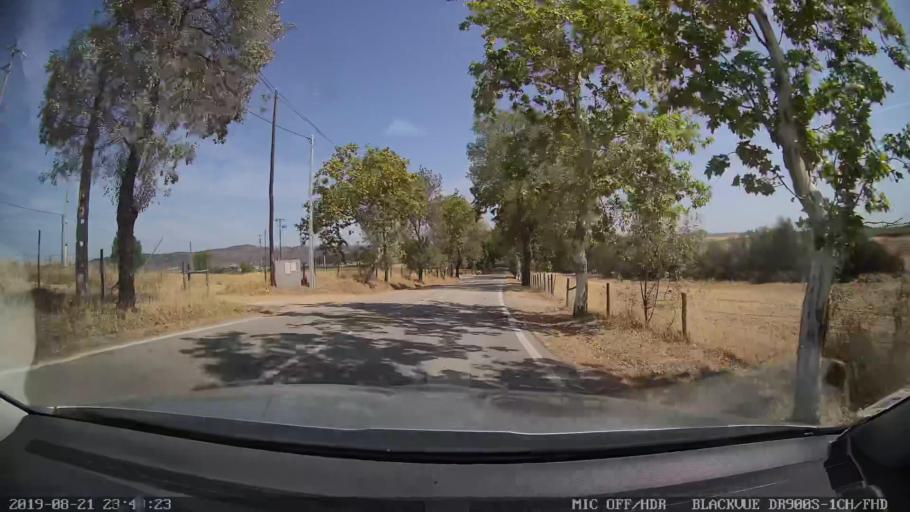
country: PT
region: Castelo Branco
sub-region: Idanha-A-Nova
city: Idanha-a-Nova
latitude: 39.8773
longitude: -7.2509
